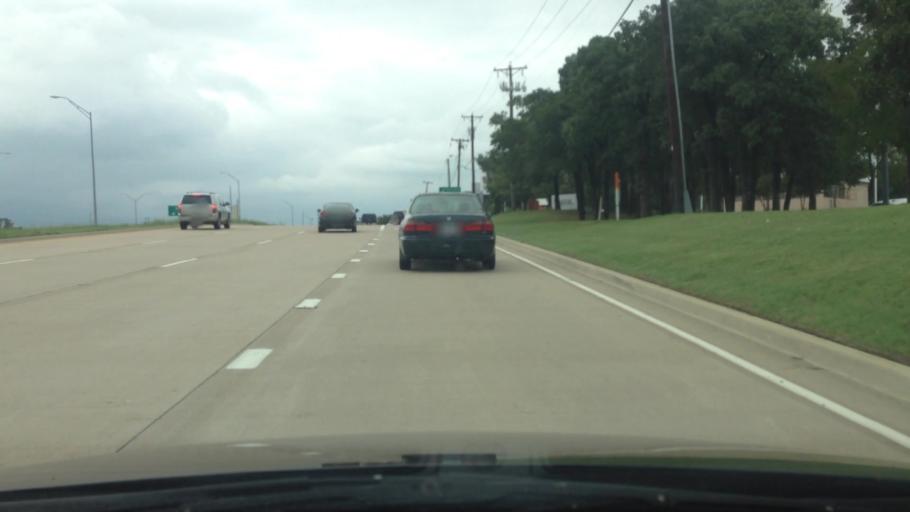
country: US
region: Texas
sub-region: Tarrant County
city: Grapevine
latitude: 32.9369
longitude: -97.0979
